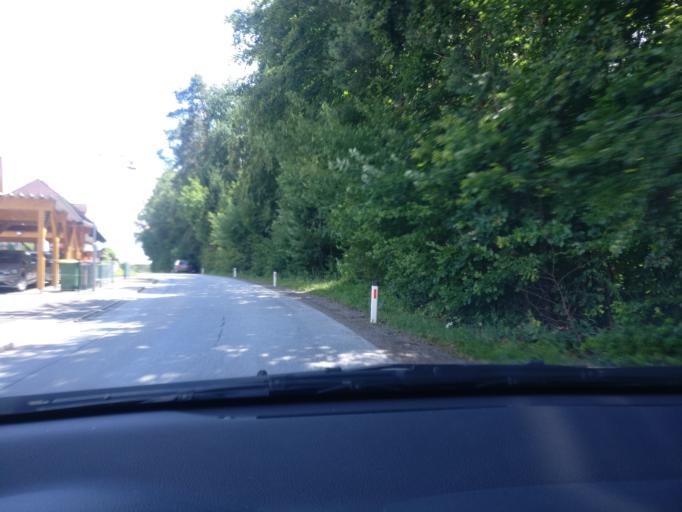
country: AT
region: Styria
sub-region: Politischer Bezirk Weiz
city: Nitscha
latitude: 47.1281
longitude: 15.7316
